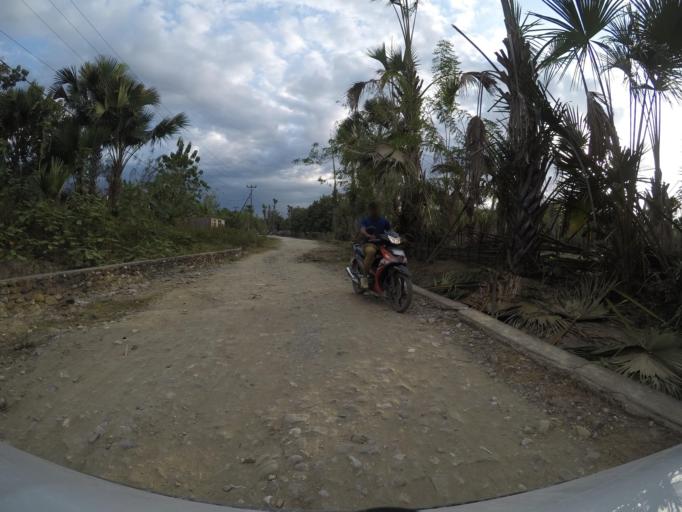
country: TL
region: Bobonaro
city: Maliana
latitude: -8.8649
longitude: 125.2152
